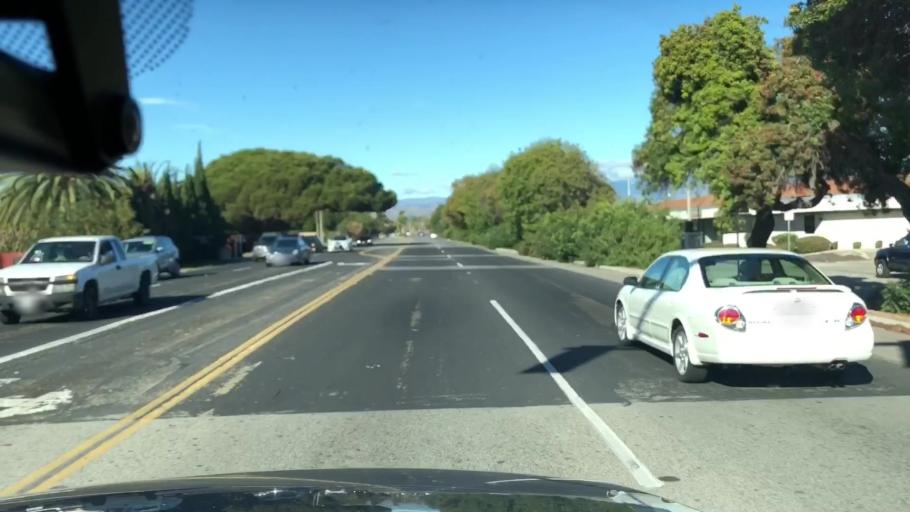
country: US
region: California
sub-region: Ventura County
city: Oxnard
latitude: 34.2117
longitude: -119.1946
